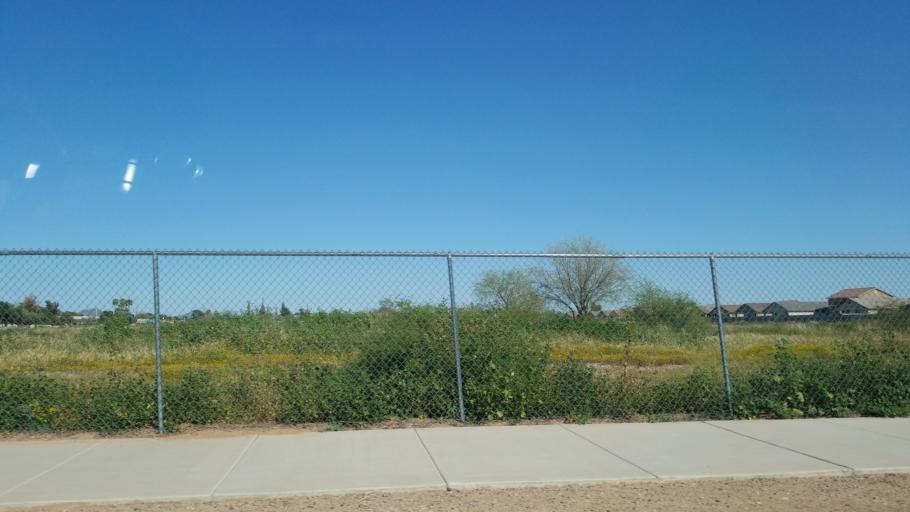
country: US
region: Arizona
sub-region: Maricopa County
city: Glendale
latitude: 33.5629
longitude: -112.1949
